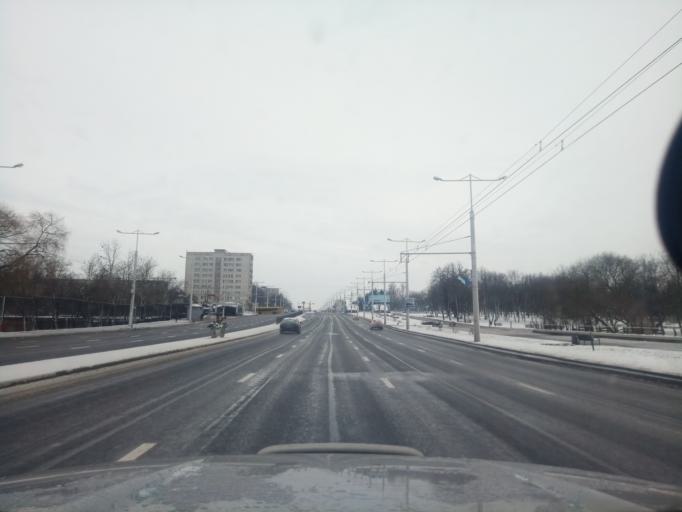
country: BY
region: Minsk
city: Hatava
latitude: 53.8512
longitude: 27.6335
